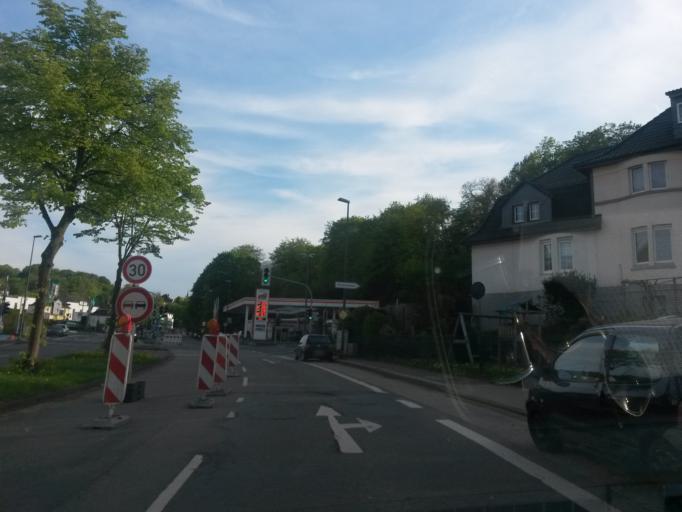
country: DE
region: North Rhine-Westphalia
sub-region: Regierungsbezirk Arnsberg
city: Luedenscheid
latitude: 51.2243
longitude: 7.6318
